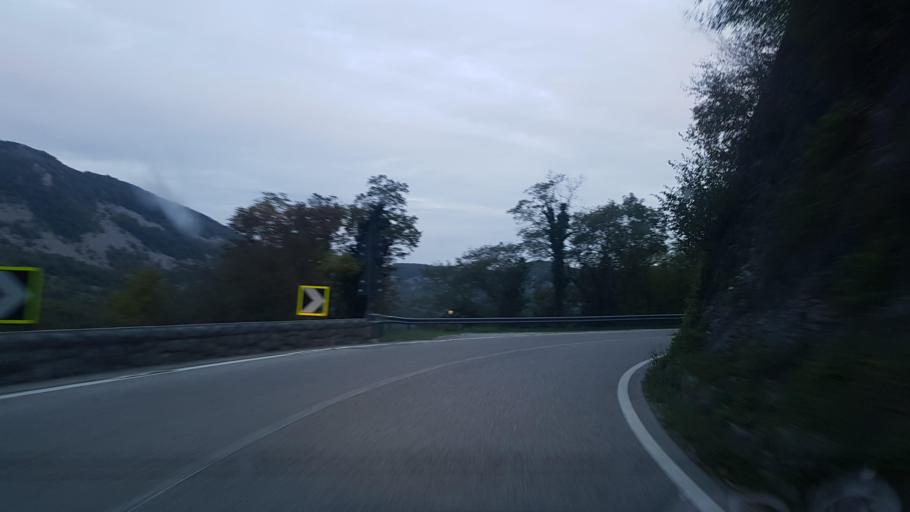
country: IT
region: Friuli Venezia Giulia
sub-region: Provincia di Pordenone
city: Anduins
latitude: 46.2413
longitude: 12.9726
